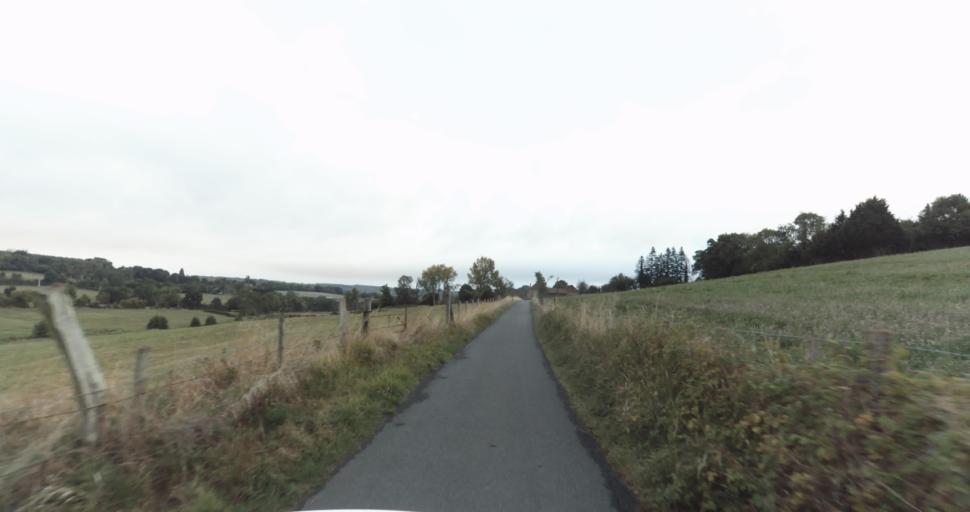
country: FR
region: Lower Normandy
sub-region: Departement de l'Orne
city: Vimoutiers
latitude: 48.9122
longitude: 0.1082
